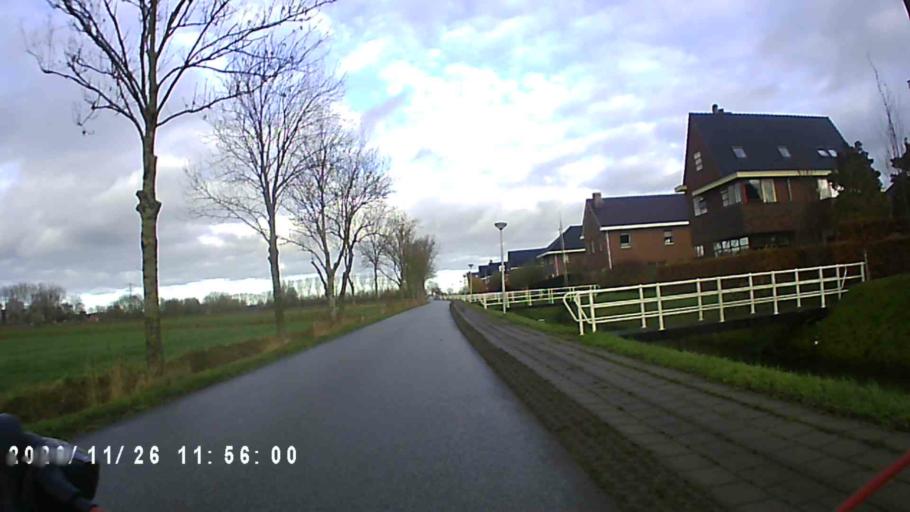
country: NL
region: Groningen
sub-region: Gemeente Bedum
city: Bedum
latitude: 53.3065
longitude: 6.6053
